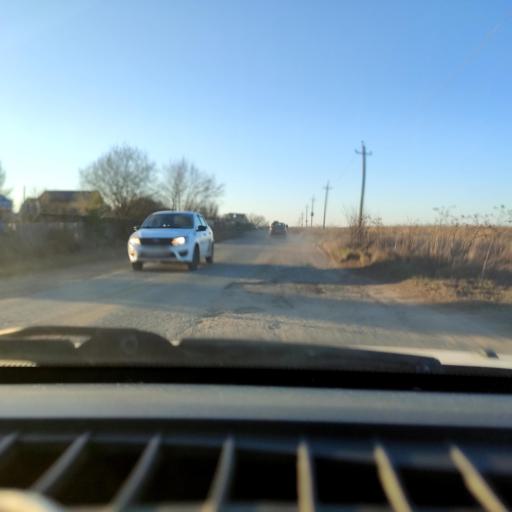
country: RU
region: Perm
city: Kultayevo
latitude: 57.9354
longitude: 56.0131
